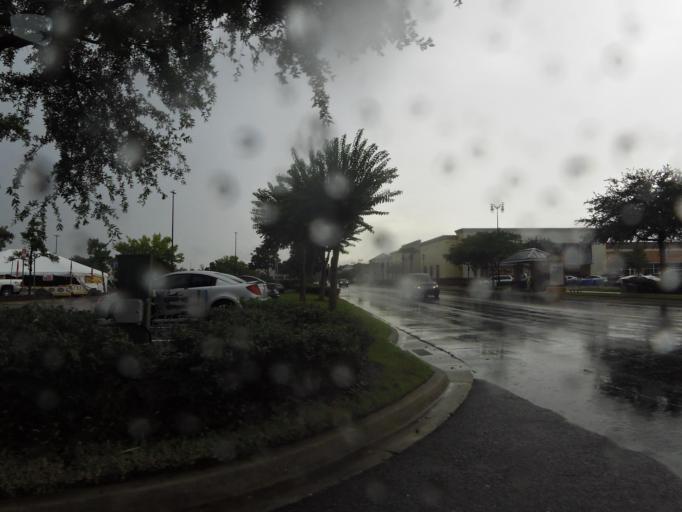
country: US
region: Florida
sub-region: Duval County
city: Jacksonville
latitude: 30.4785
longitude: -81.6404
